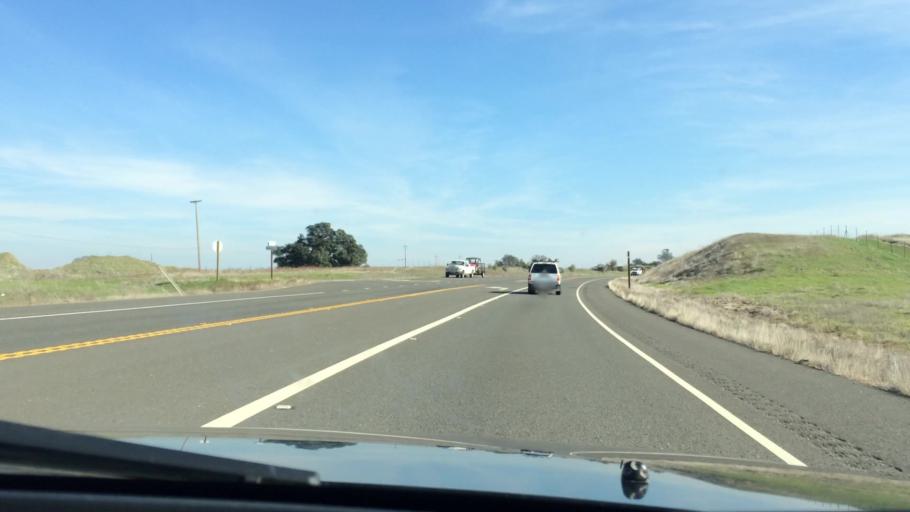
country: US
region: California
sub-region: Sacramento County
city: Rancho Murieta
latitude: 38.4858
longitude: -121.0539
